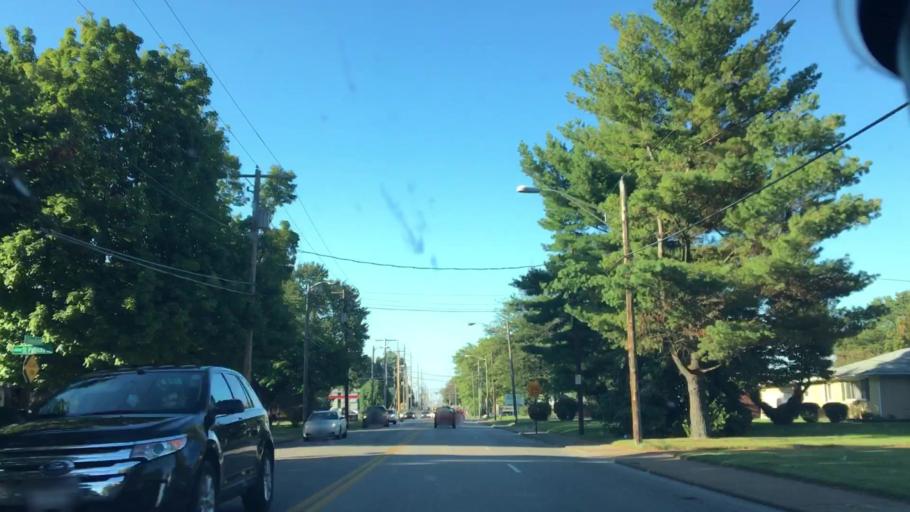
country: US
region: Indiana
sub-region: Vanderburgh County
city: Evansville
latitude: 37.9522
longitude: -87.4929
